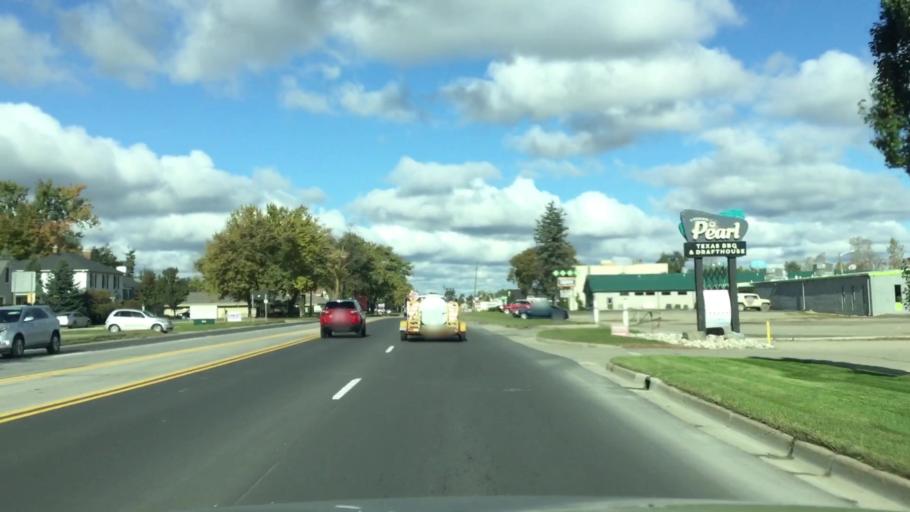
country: US
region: Michigan
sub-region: Oakland County
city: Oxford
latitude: 42.8116
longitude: -83.2527
